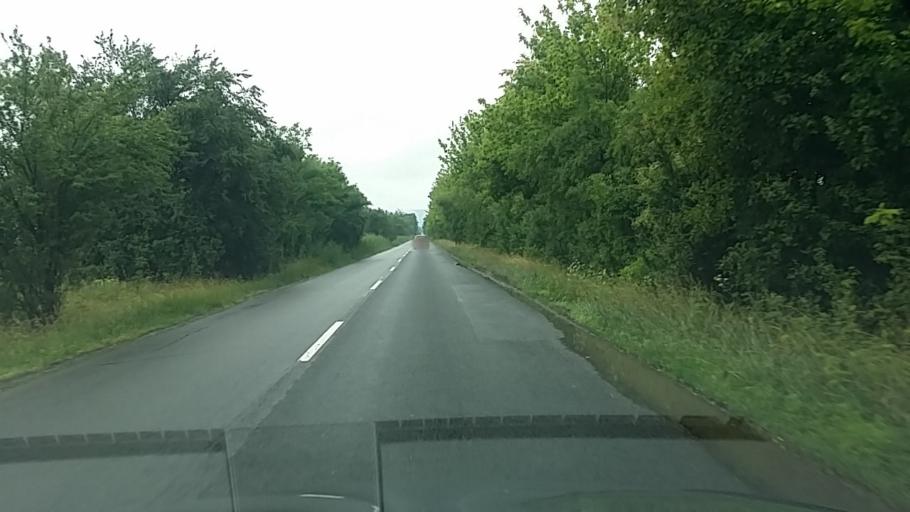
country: HU
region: Komarom-Esztergom
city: Esztergom
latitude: 47.9095
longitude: 18.7747
